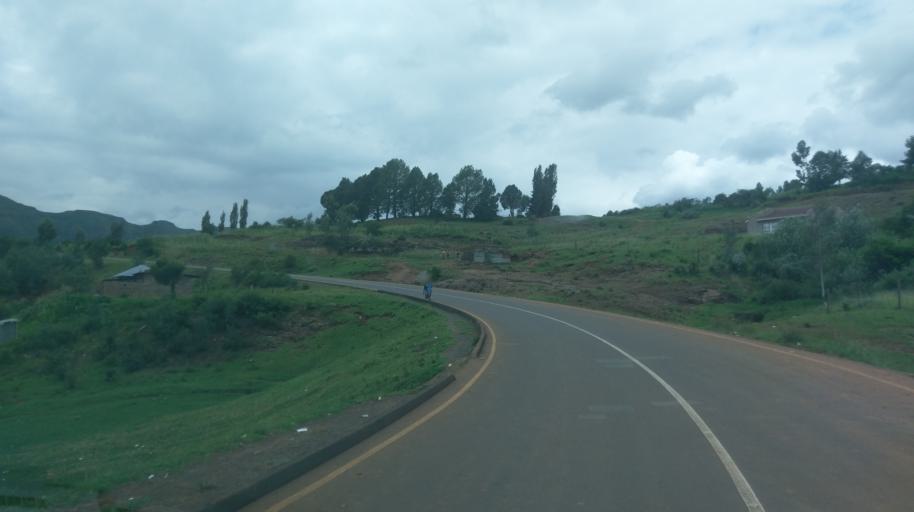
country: LS
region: Butha-Buthe
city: Butha-Buthe
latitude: -29.0358
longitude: 28.2833
